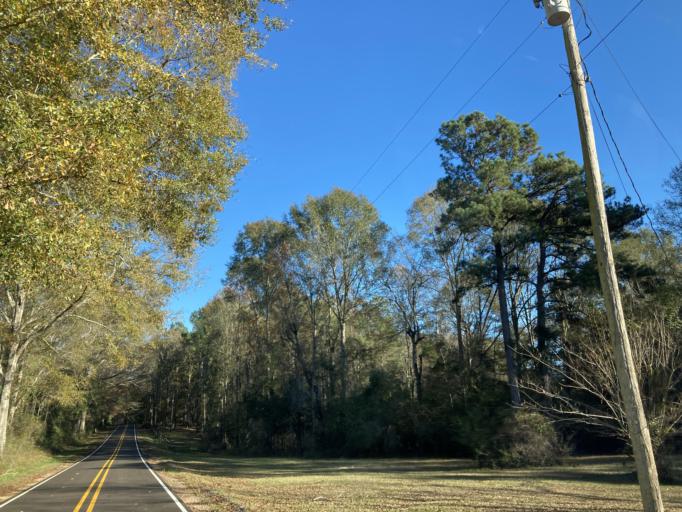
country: US
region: Mississippi
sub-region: Lamar County
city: Sumrall
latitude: 31.3537
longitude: -89.5730
